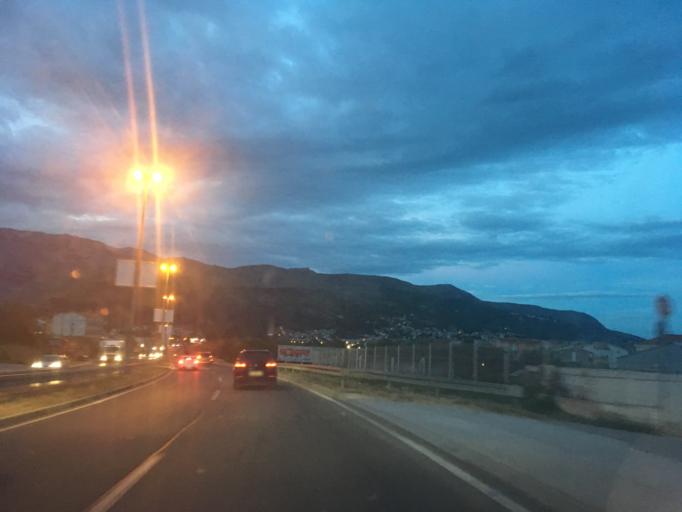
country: HR
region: Splitsko-Dalmatinska
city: Kamen
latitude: 43.5051
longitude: 16.5124
